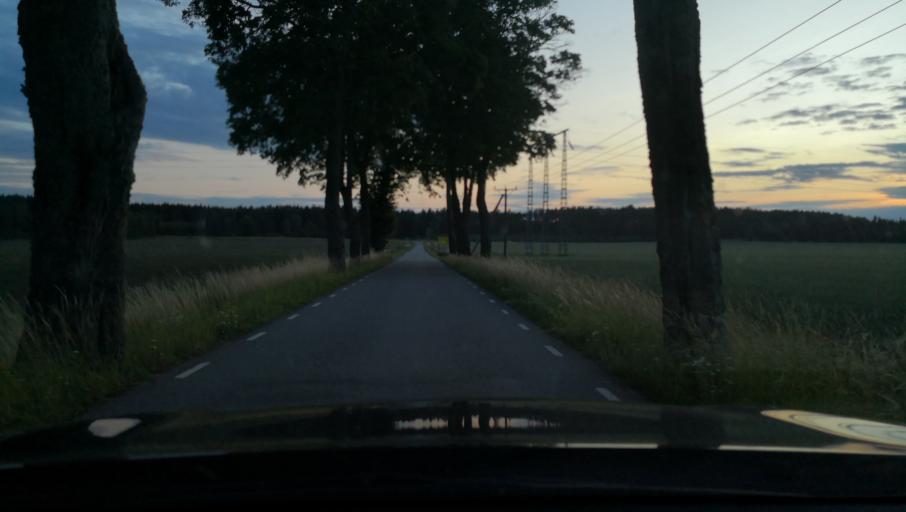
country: SE
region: Uppsala
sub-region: Osthammars Kommun
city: Bjorklinge
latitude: 60.0623
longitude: 17.5549
